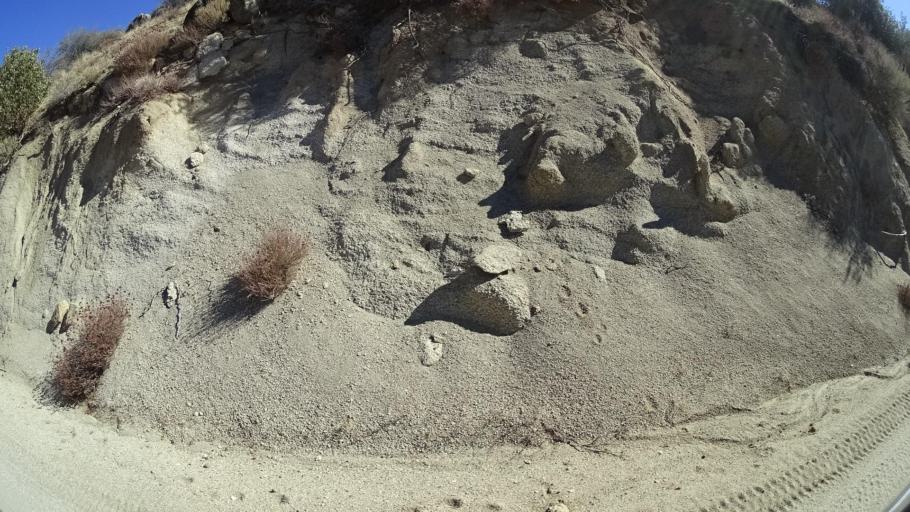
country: US
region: California
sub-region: Kern County
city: Wofford Heights
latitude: 35.7048
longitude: -118.4946
